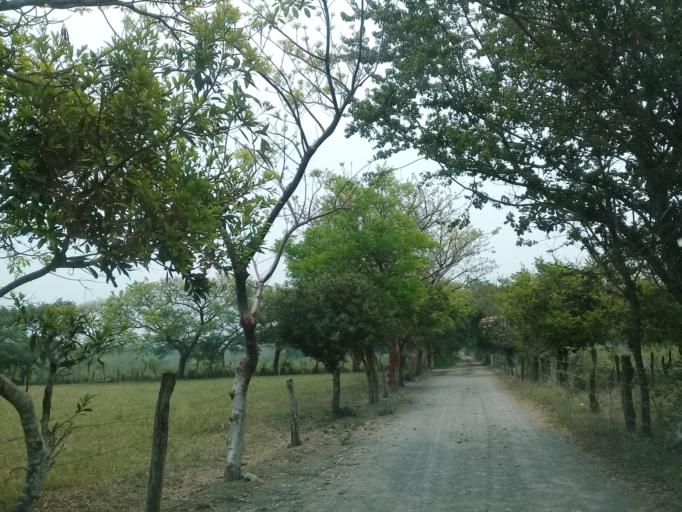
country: MX
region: Veracruz
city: Jamapa
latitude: 18.9555
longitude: -96.2000
